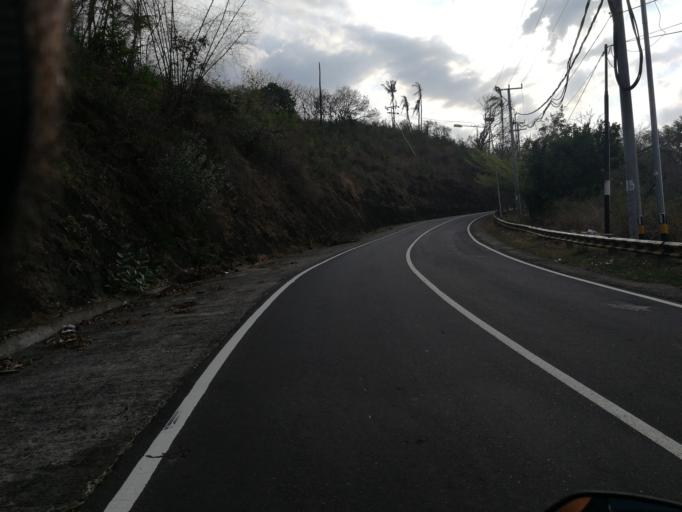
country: ID
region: West Nusa Tenggara
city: Karangsubagan
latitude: -8.4365
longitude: 116.0413
